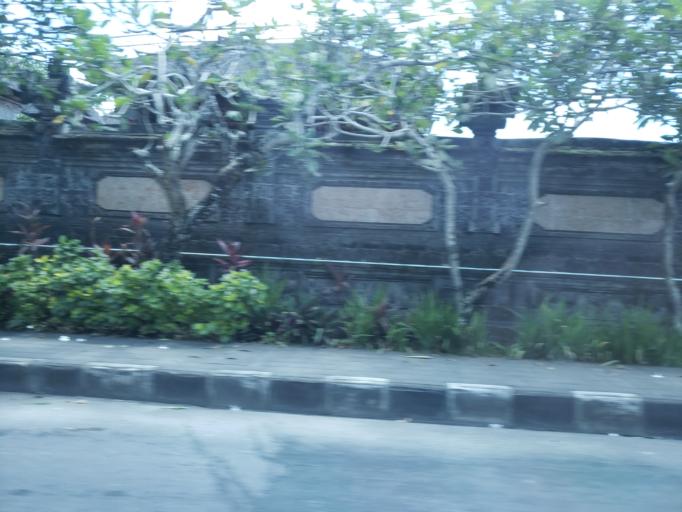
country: ID
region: Bali
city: Kangin
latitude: -8.8313
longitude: 115.1265
